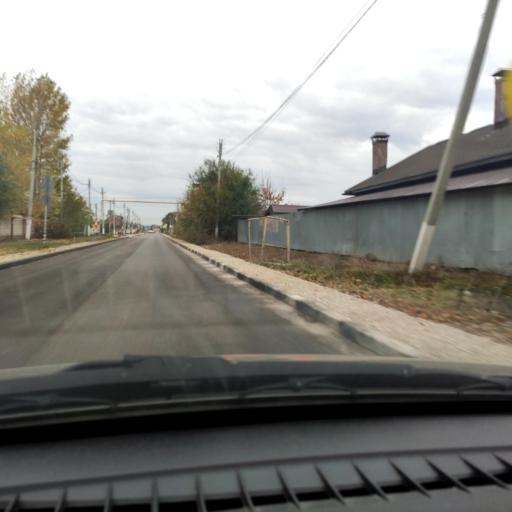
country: RU
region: Samara
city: Podstepki
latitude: 53.5120
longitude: 49.2331
